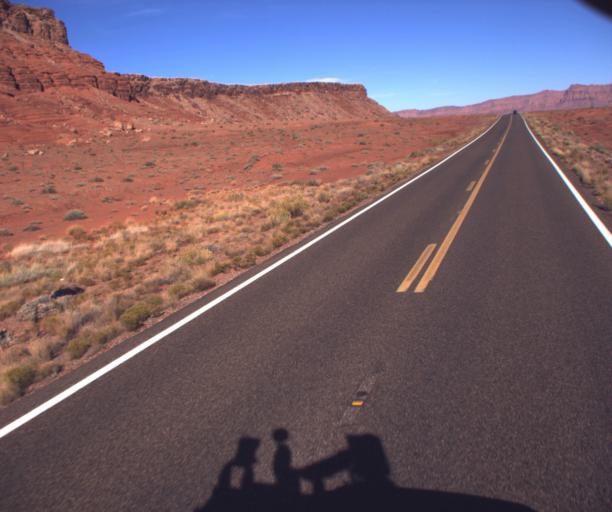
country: US
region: Arizona
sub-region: Coconino County
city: Page
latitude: 36.7488
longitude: -111.7361
